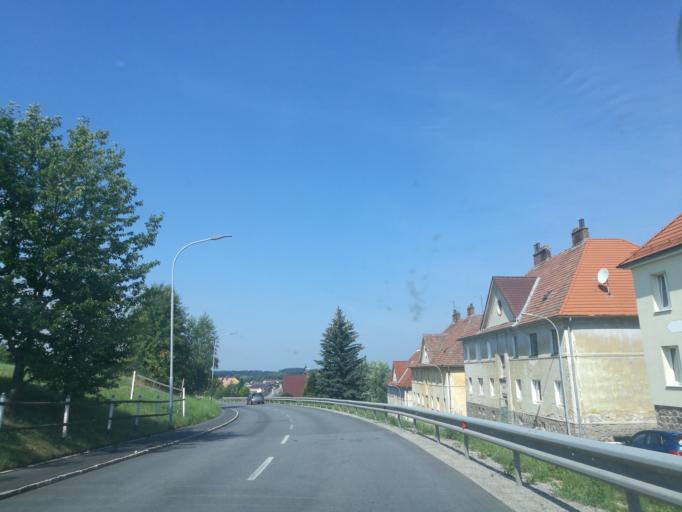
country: AT
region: Lower Austria
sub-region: Politischer Bezirk Gmund
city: Heidenreichstein
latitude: 48.8650
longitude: 15.1308
